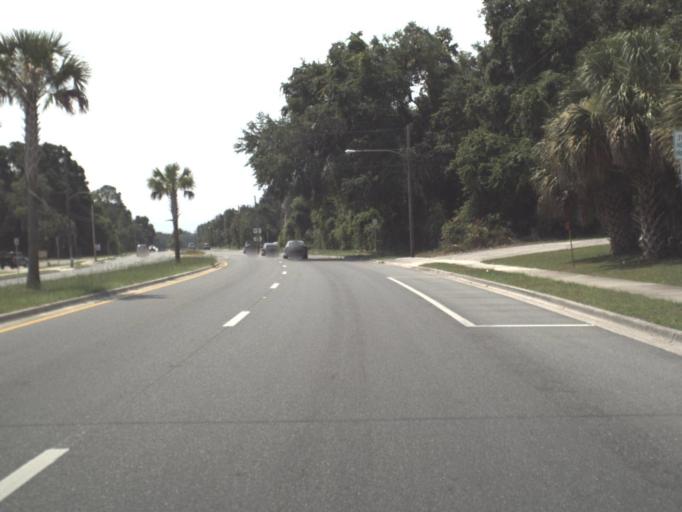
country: US
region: Florida
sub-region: Levy County
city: Chiefland
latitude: 29.4723
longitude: -82.8591
